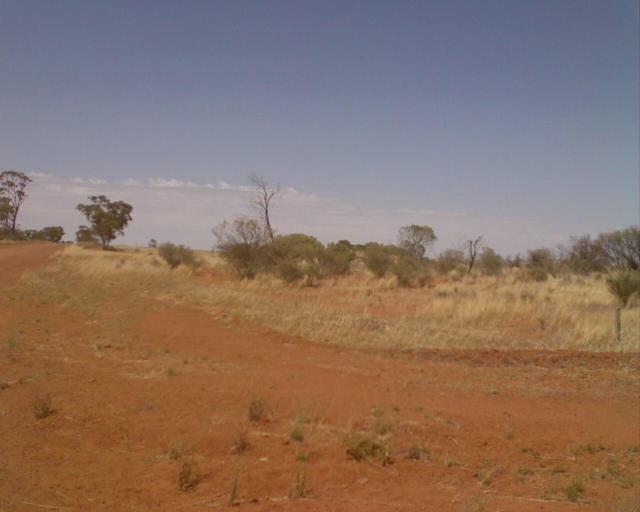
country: AU
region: Western Australia
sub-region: Merredin
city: Merredin
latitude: -30.9278
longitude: 118.2889
